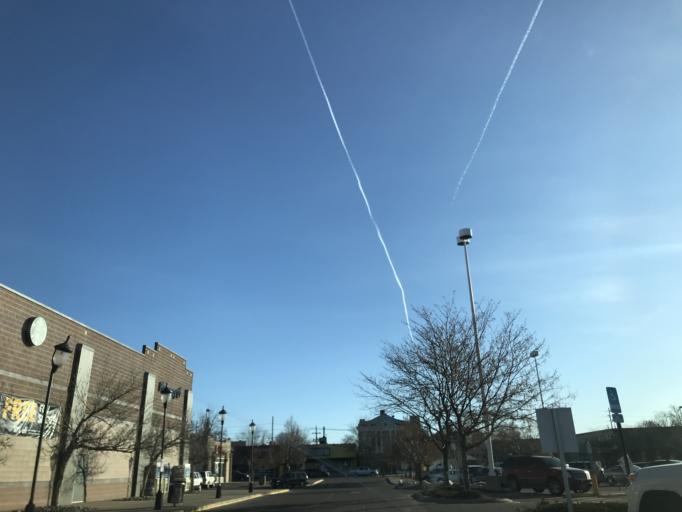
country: US
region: Colorado
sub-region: Denver County
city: Denver
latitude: 39.7102
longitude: -104.9888
